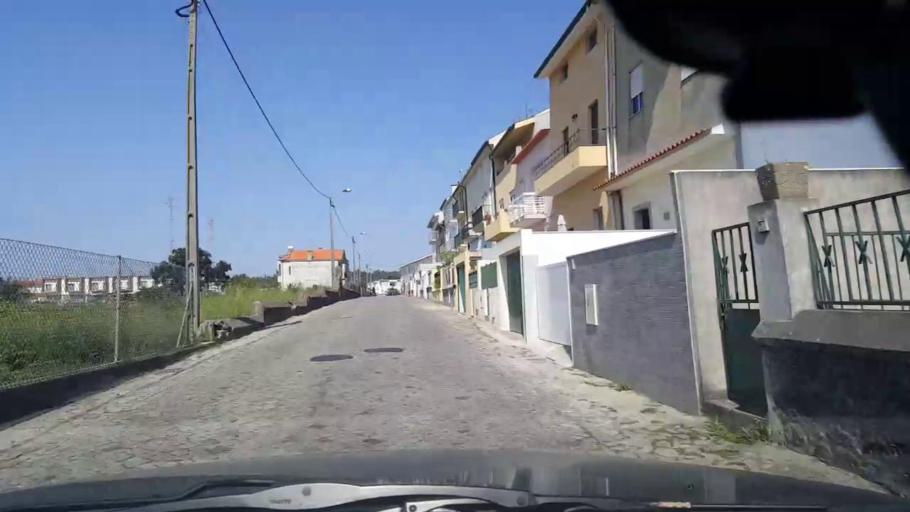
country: PT
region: Porto
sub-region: Vila do Conde
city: Vila do Conde
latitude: 41.3590
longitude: -8.7275
